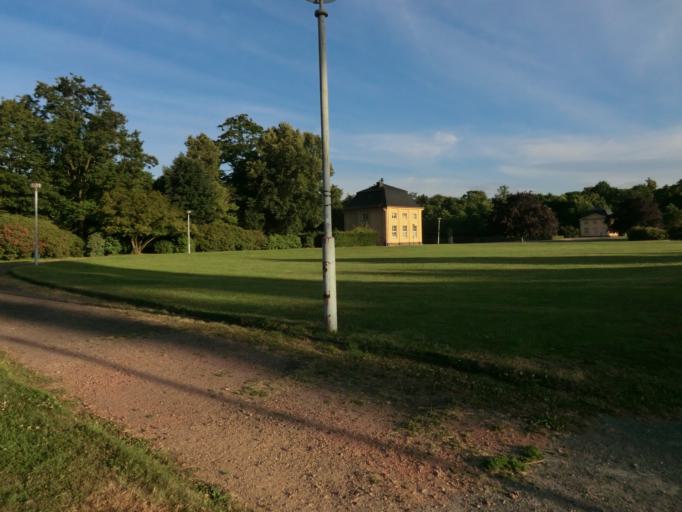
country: DE
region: Saxony
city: Dresden
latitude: 51.0389
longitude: 13.7640
